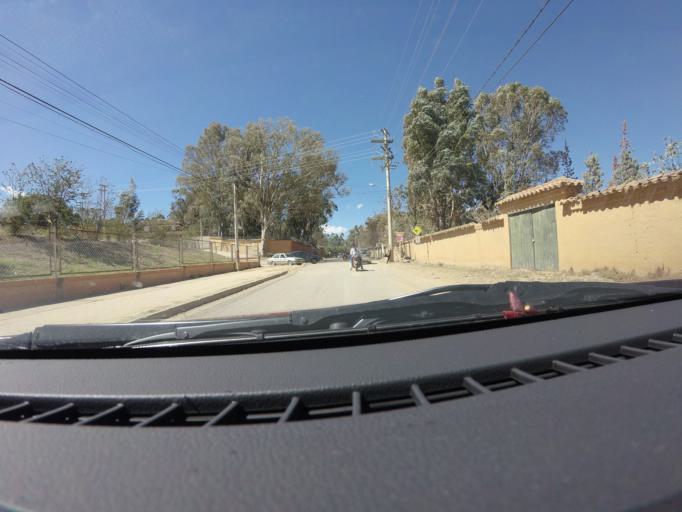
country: CO
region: Boyaca
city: Villa de Leiva
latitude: 5.6320
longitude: -73.5309
